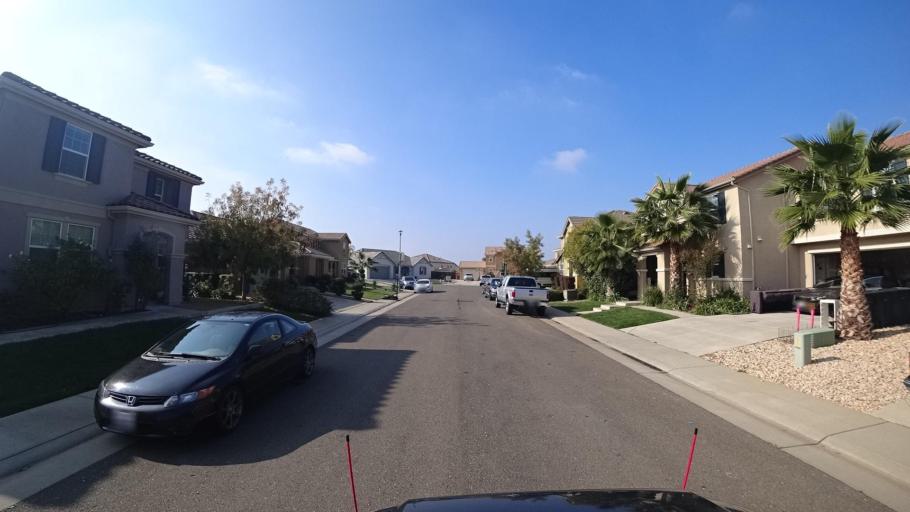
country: US
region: California
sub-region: Sacramento County
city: Vineyard
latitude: 38.4475
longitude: -121.3649
